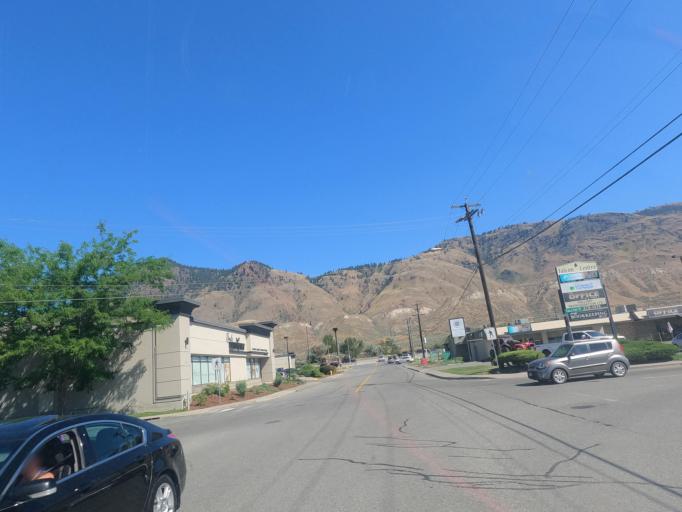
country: CA
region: British Columbia
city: Kamloops
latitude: 50.6789
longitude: -120.2723
